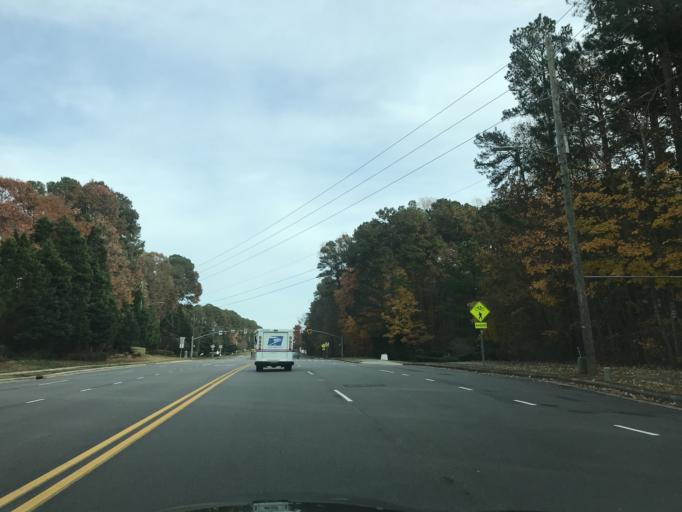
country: US
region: North Carolina
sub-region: Wake County
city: West Raleigh
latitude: 35.8944
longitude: -78.6353
